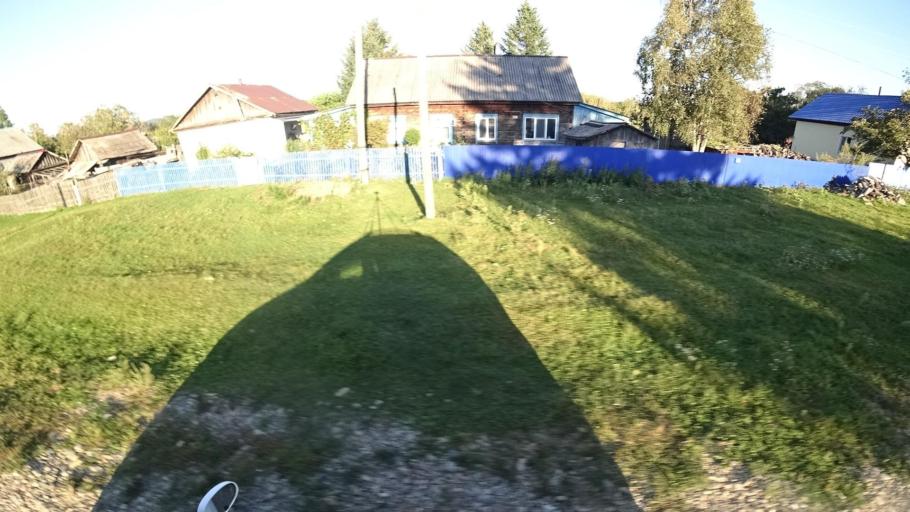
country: RU
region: Primorskiy
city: Kirovskiy
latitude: 44.8308
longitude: 133.5727
